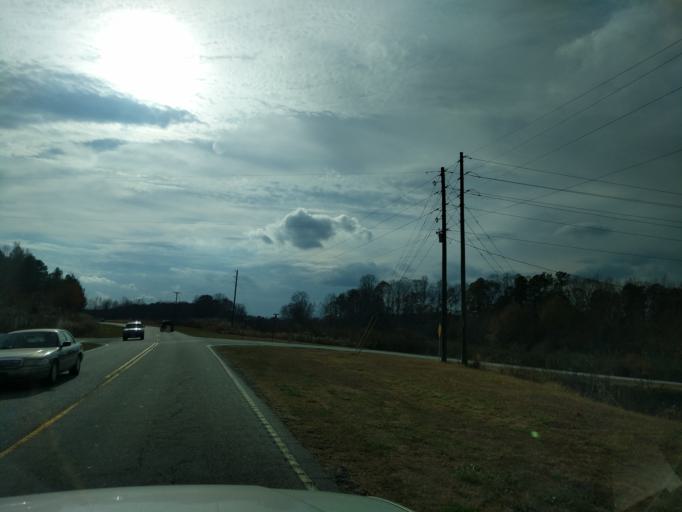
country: US
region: South Carolina
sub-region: Oconee County
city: Westminster
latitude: 34.6532
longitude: -83.0467
